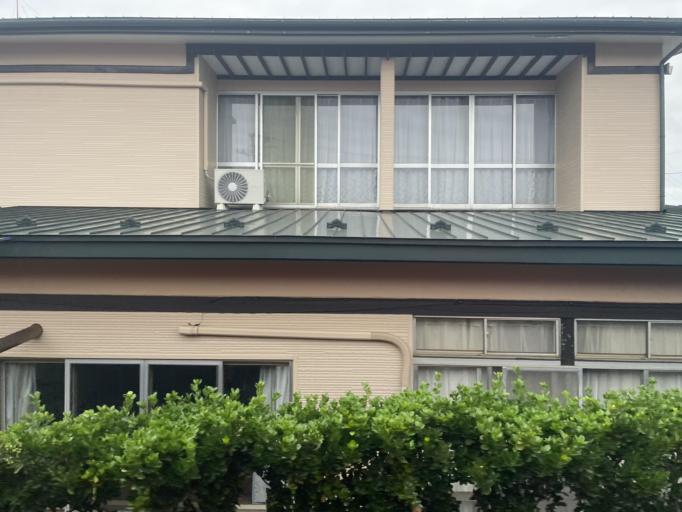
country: JP
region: Akita
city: Tenno
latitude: 39.8987
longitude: 139.9641
